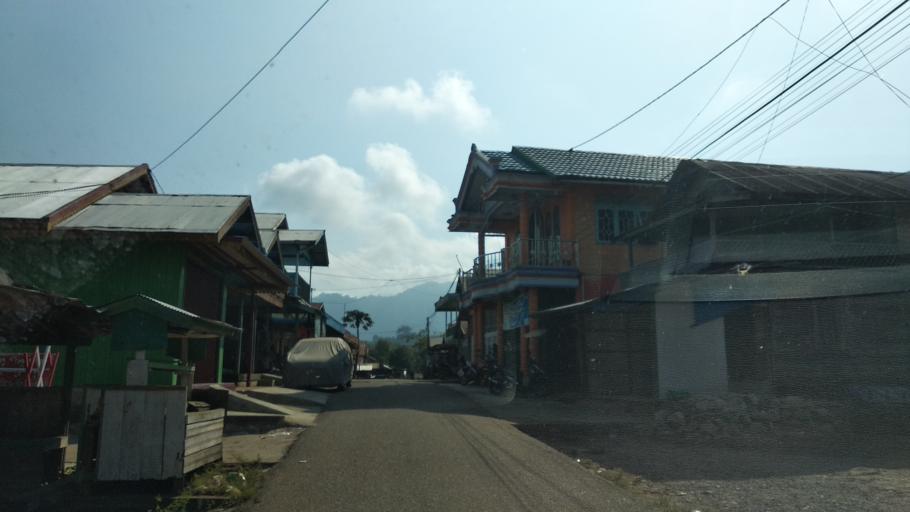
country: ID
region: East Kalimantan
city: Muarakomam
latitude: -1.6859
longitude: 115.8177
